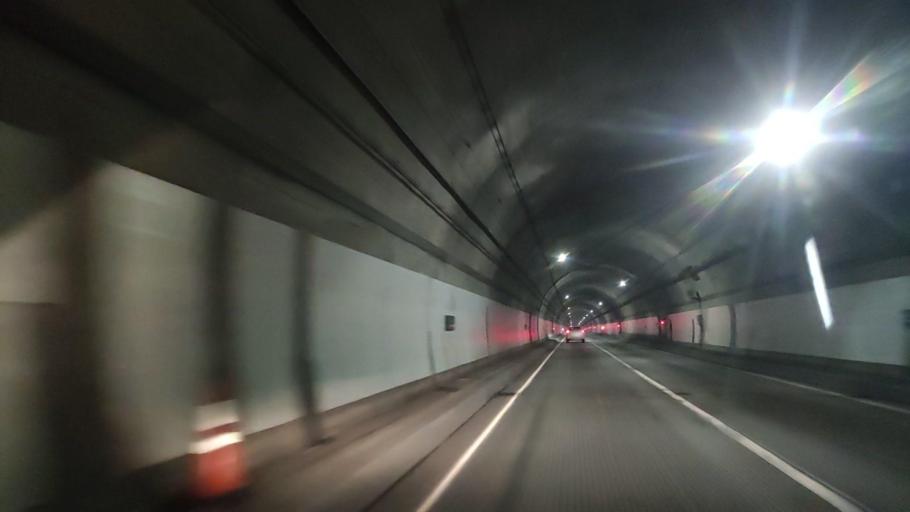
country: JP
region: Hokkaido
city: Rumoi
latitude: 43.7102
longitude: 141.3324
